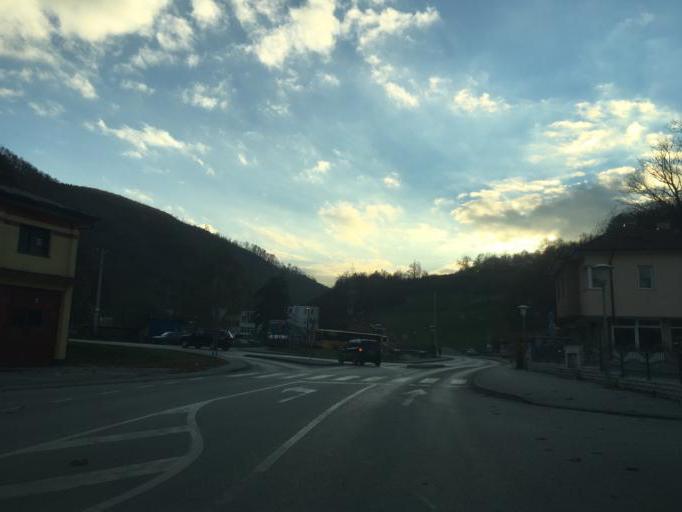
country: BA
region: Federation of Bosnia and Herzegovina
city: Novi Travnik
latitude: 44.1675
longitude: 17.6520
